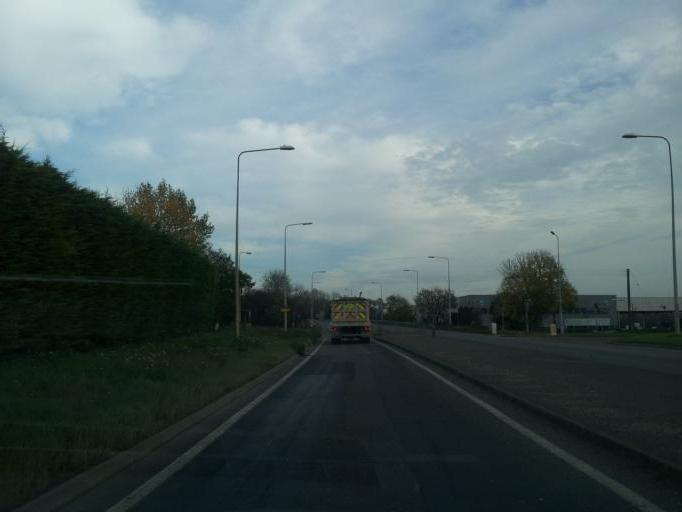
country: GB
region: England
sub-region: Cambridgeshire
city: Duxford
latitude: 52.1022
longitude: 0.1592
